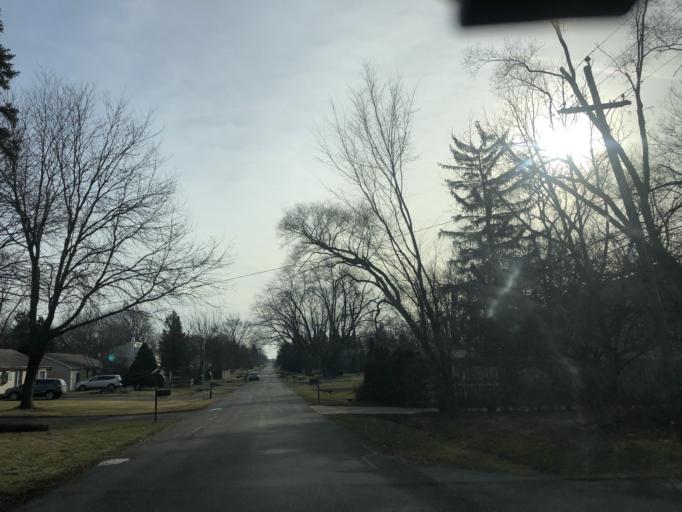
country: US
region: Illinois
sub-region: Cook County
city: Lemont
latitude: 41.7129
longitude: -88.0099
